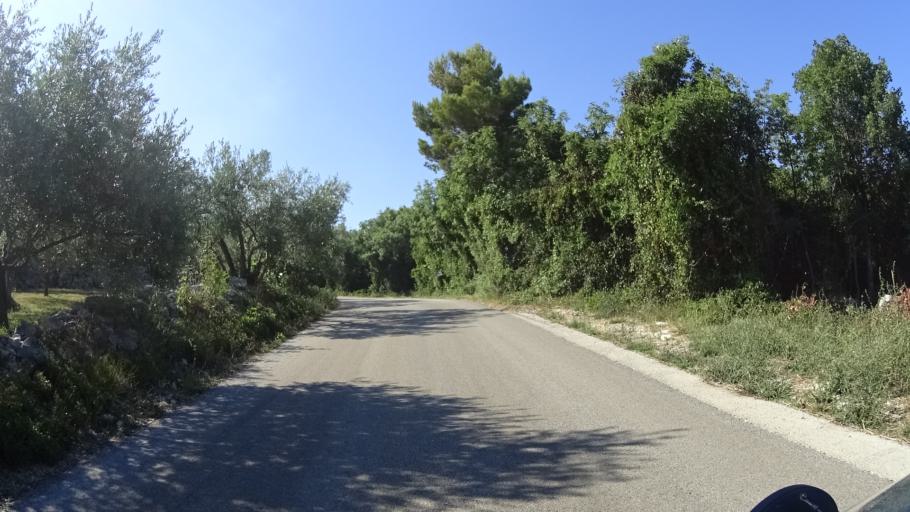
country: HR
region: Istarska
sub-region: Grad Labin
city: Rabac
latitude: 45.0087
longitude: 14.1609
